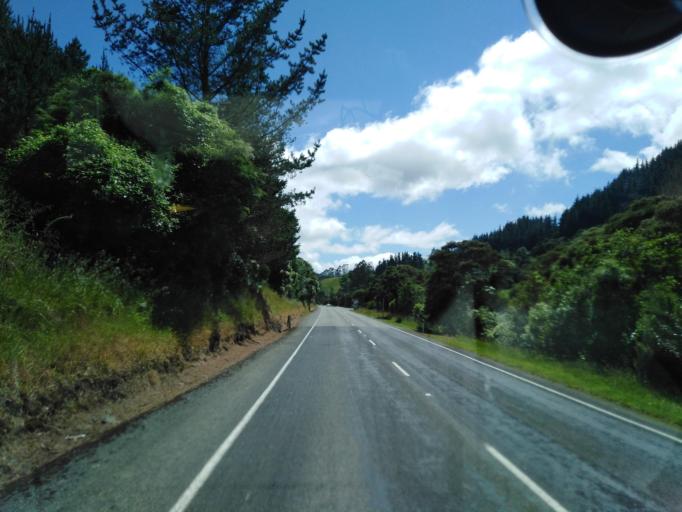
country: NZ
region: Nelson
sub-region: Nelson City
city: Nelson
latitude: -41.2248
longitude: 173.3961
